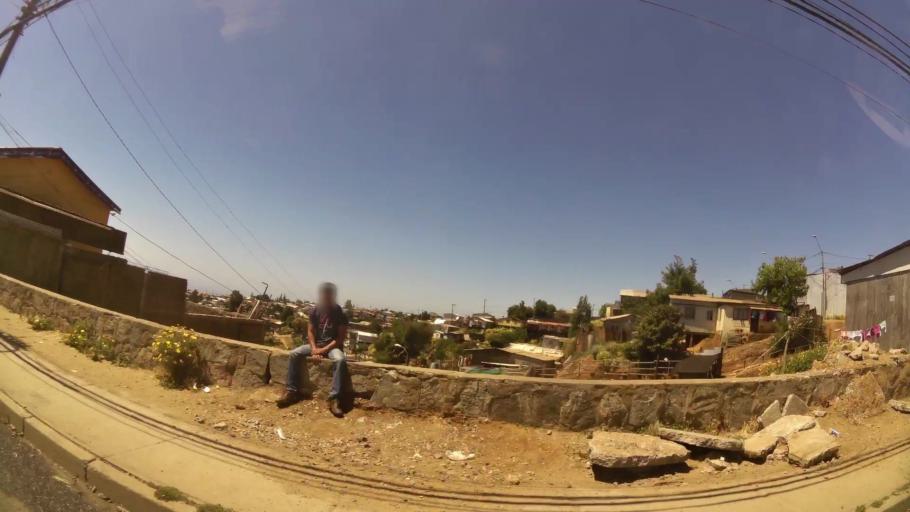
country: CL
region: Valparaiso
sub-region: Provincia de Valparaiso
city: Valparaiso
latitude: -33.0597
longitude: -71.6423
